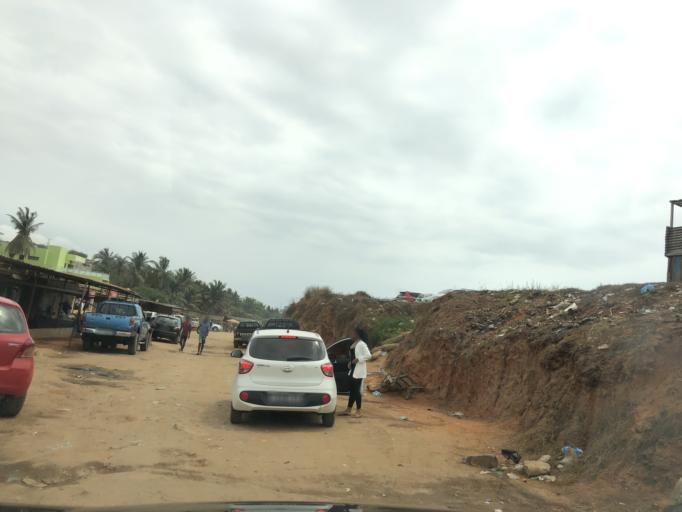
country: AO
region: Luanda
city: Luanda
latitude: -8.8709
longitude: 13.1950
